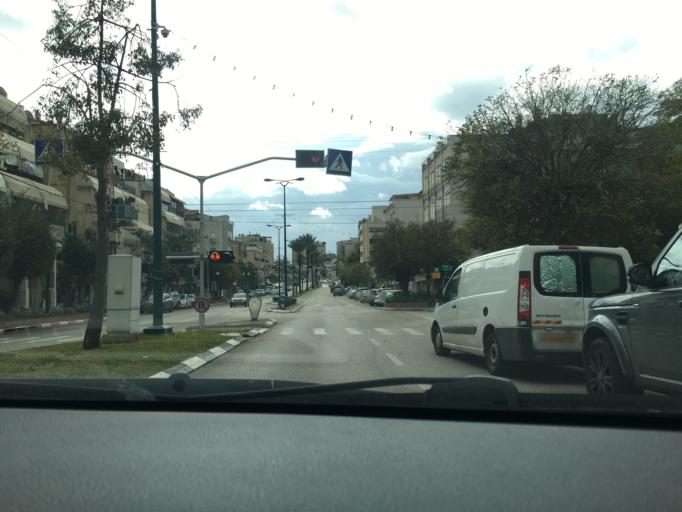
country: IL
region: Tel Aviv
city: Ramat HaSharon
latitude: 32.1399
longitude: 34.8423
